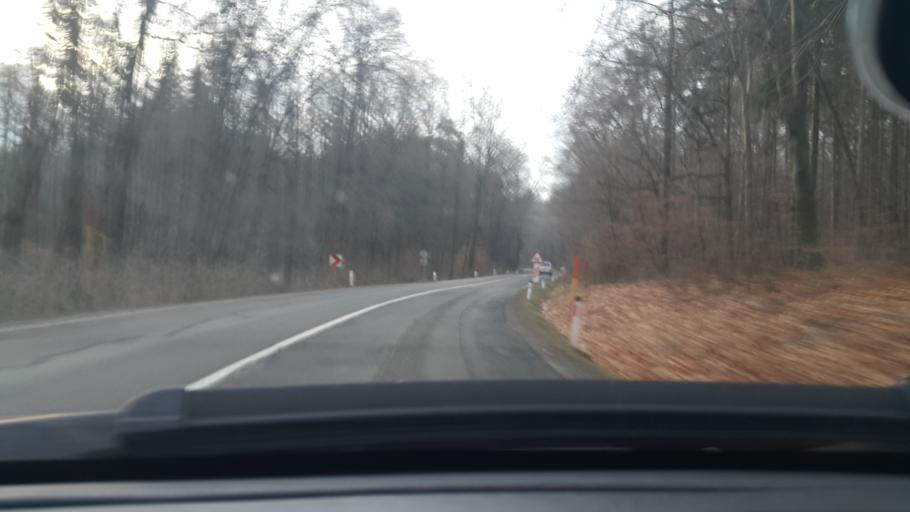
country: SI
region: Slovenska Bistrica
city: Slovenska Bistrica
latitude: 46.3598
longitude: 15.5698
